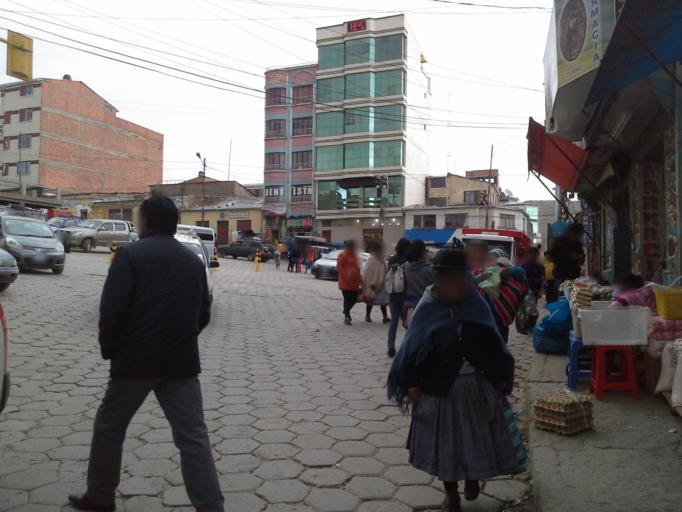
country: BO
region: Potosi
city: Llallagua
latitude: -18.4231
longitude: -66.5860
